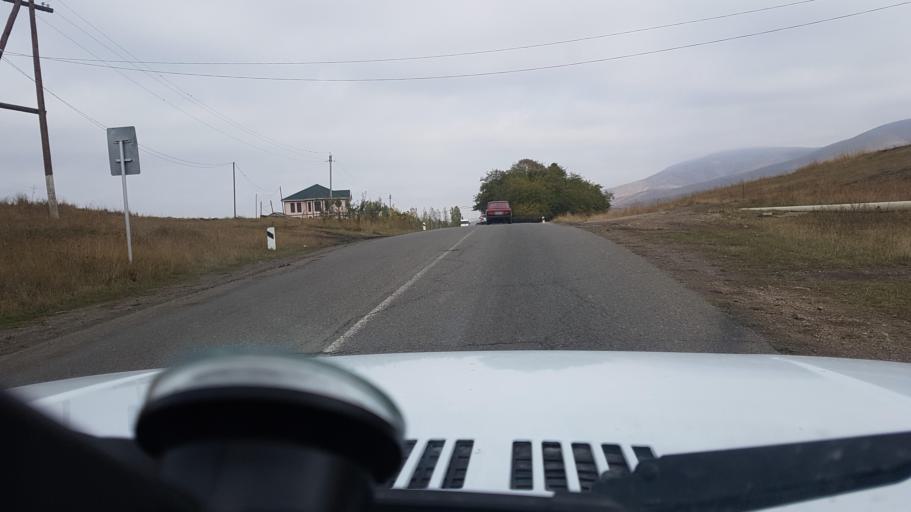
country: AZ
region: Gadabay Rayon
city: Ariqdam
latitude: 40.6194
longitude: 45.8124
